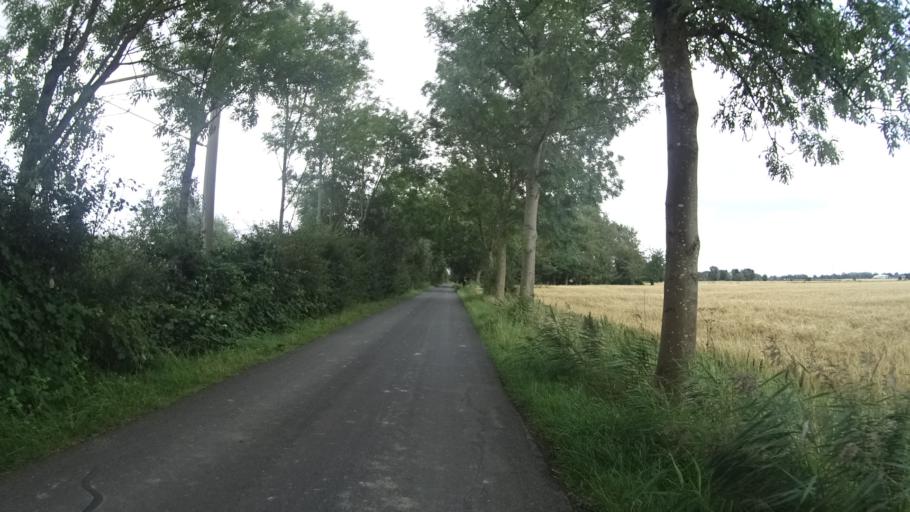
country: DE
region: Schleswig-Holstein
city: Gluckstadt
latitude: 53.7827
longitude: 9.4463
